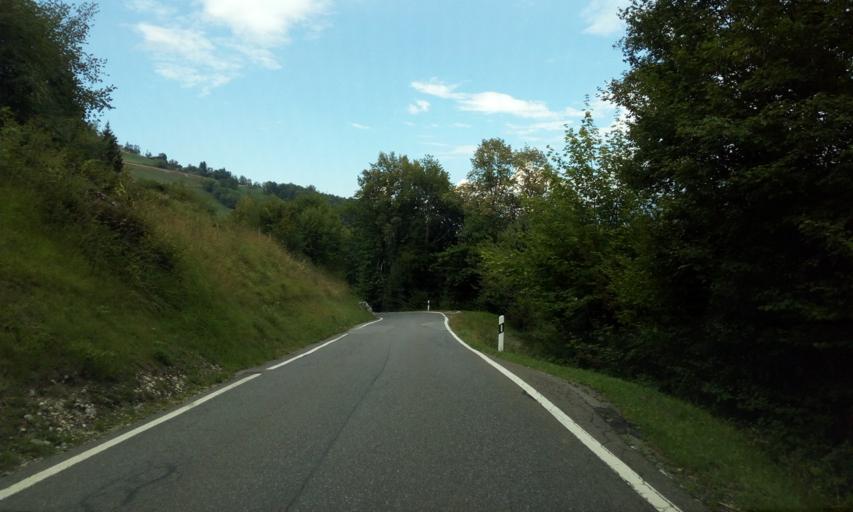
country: CH
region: Valais
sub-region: Monthey District
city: Vionnaz
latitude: 46.3068
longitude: 6.8870
